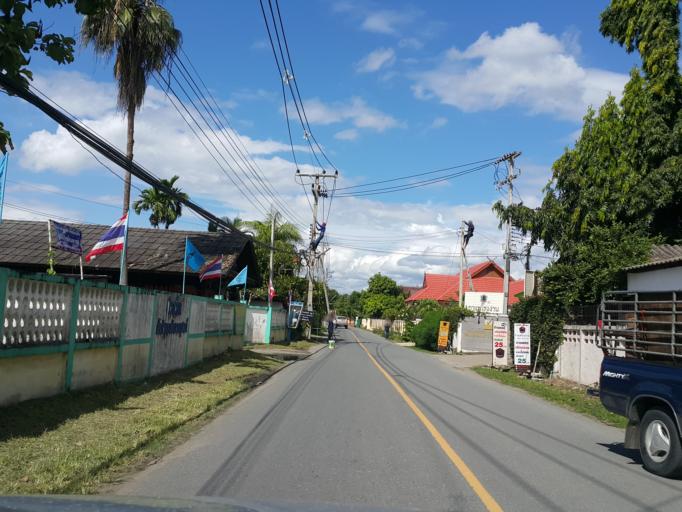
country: TH
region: Chiang Mai
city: San Kamphaeng
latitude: 18.7530
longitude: 99.1284
